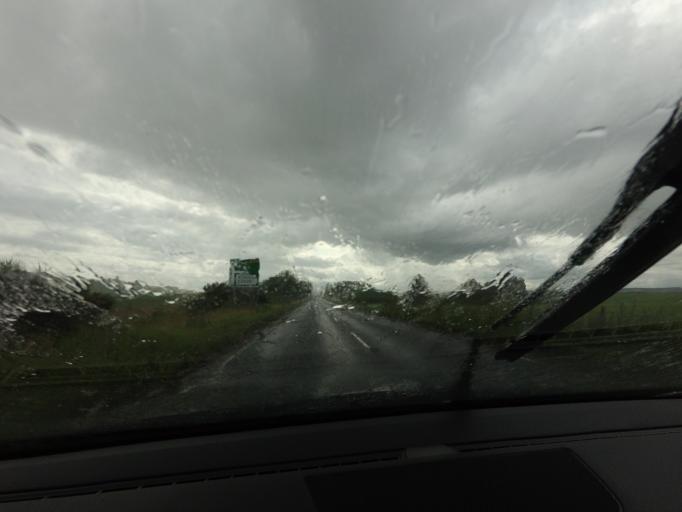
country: GB
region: Scotland
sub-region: Highland
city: Fortrose
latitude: 57.5129
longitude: -4.0953
